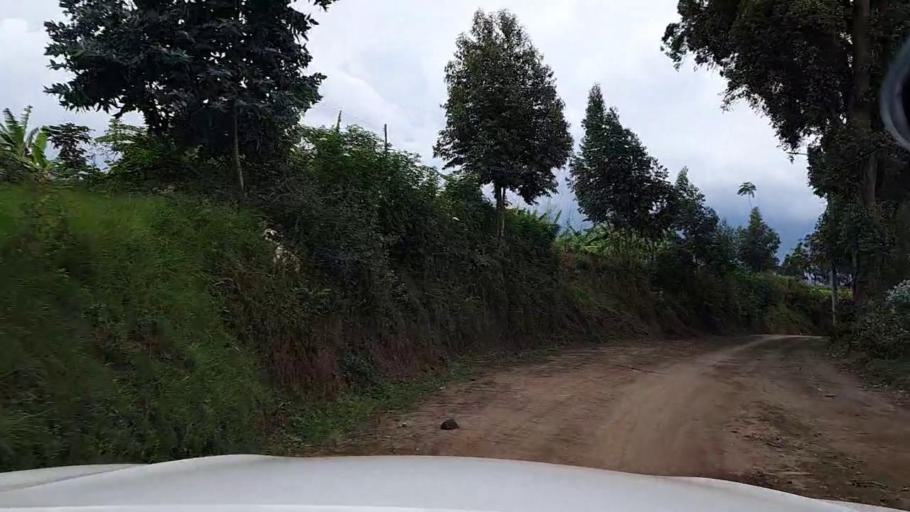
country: BI
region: Kayanza
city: Kayanza
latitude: -2.7970
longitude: 29.5070
